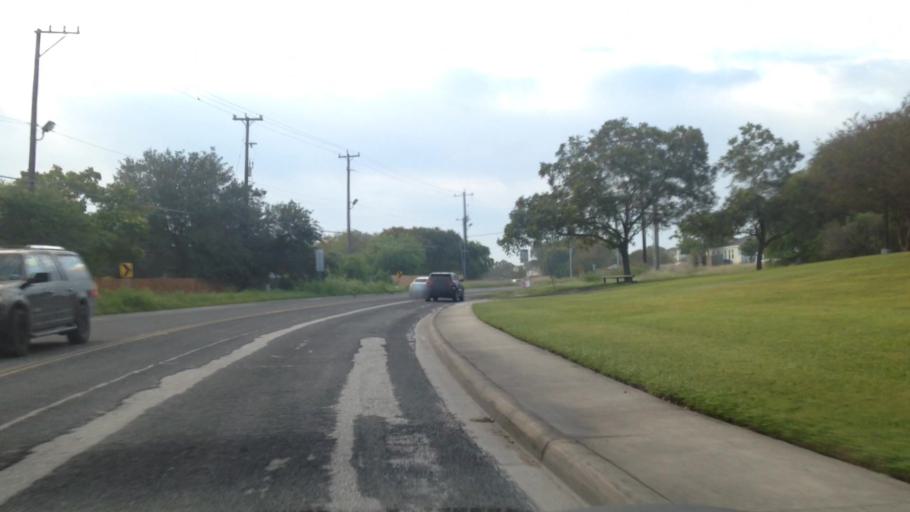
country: US
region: Texas
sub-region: Bexar County
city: Live Oak
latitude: 29.5866
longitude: -98.3773
